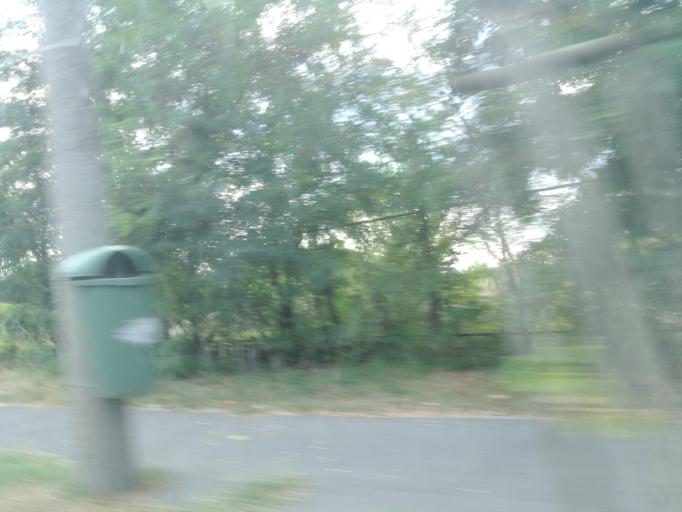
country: RO
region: Ilfov
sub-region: Comuna Mogosoaia
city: Mogosoaia
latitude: 44.5058
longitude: 26.0255
